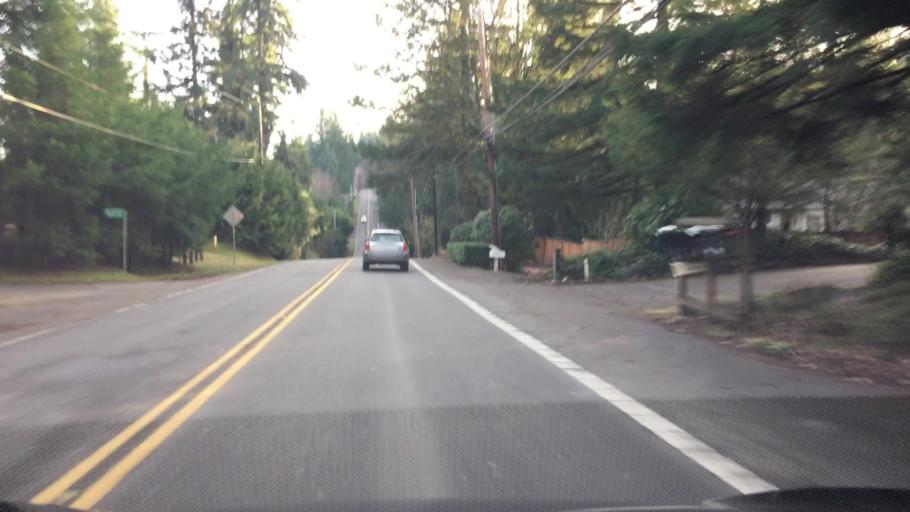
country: US
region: Washington
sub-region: King County
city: Woodinville
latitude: 47.7676
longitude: -122.1317
